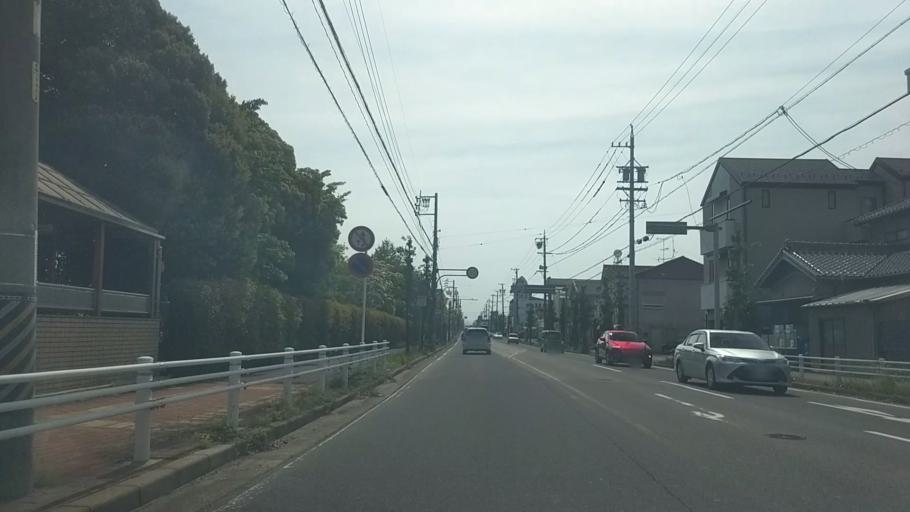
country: JP
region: Aichi
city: Anjo
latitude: 34.9526
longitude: 137.0818
